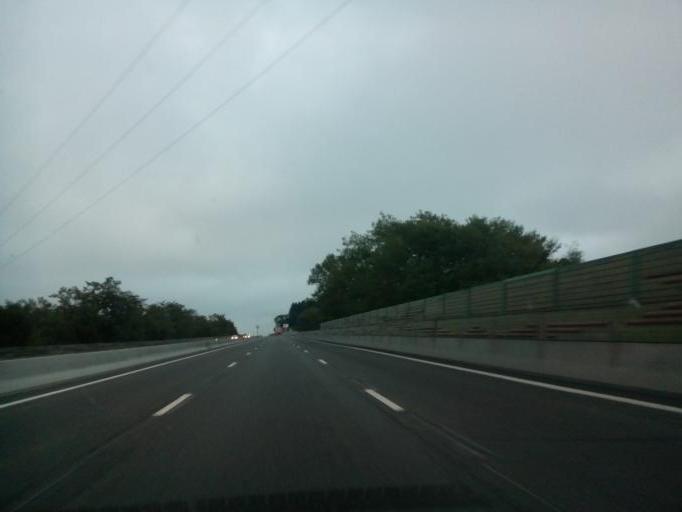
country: FR
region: Rhone-Alpes
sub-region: Departement de l'Isere
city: Saint-Jean-de-Soudain
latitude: 45.5606
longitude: 5.4303
